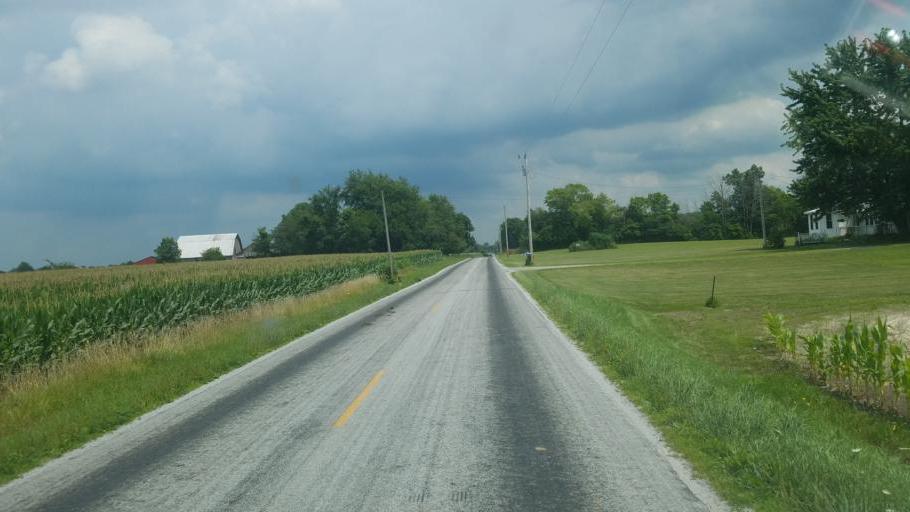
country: US
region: Ohio
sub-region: Hardin County
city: Kenton
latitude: 40.5645
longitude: -83.5199
